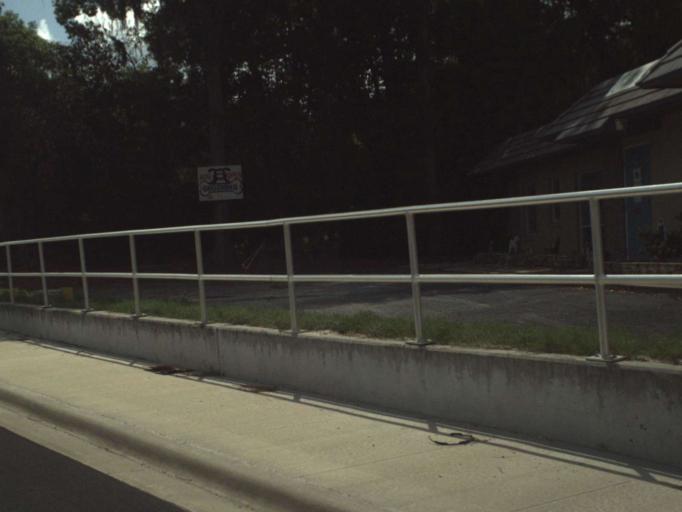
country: US
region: Florida
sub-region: Seminole County
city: Altamonte Springs
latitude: 28.6971
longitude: -81.3772
